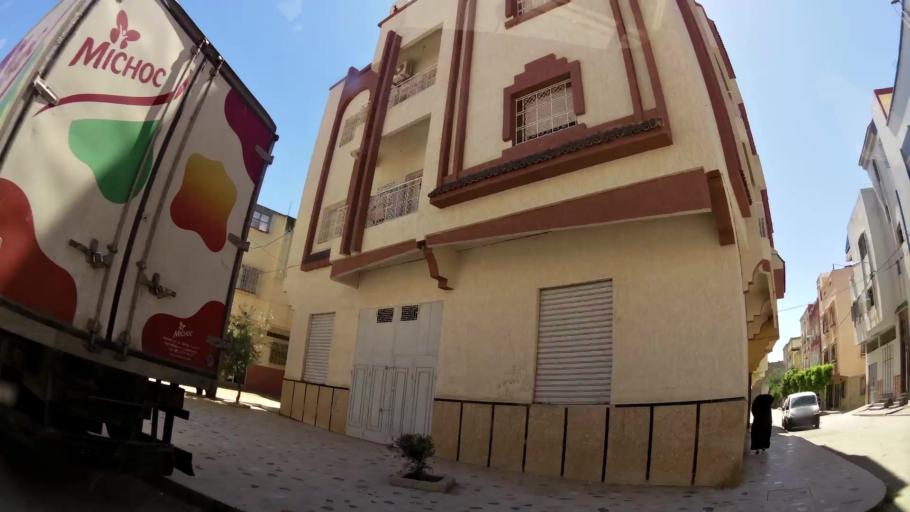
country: MA
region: Meknes-Tafilalet
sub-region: Meknes
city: Meknes
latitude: 33.8962
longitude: -5.5812
